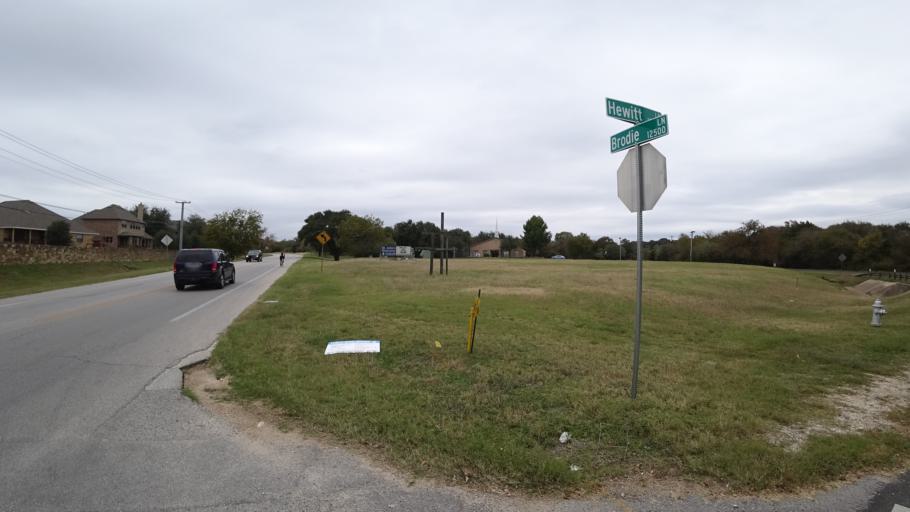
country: US
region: Texas
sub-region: Travis County
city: Manchaca
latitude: 30.1421
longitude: -97.8475
